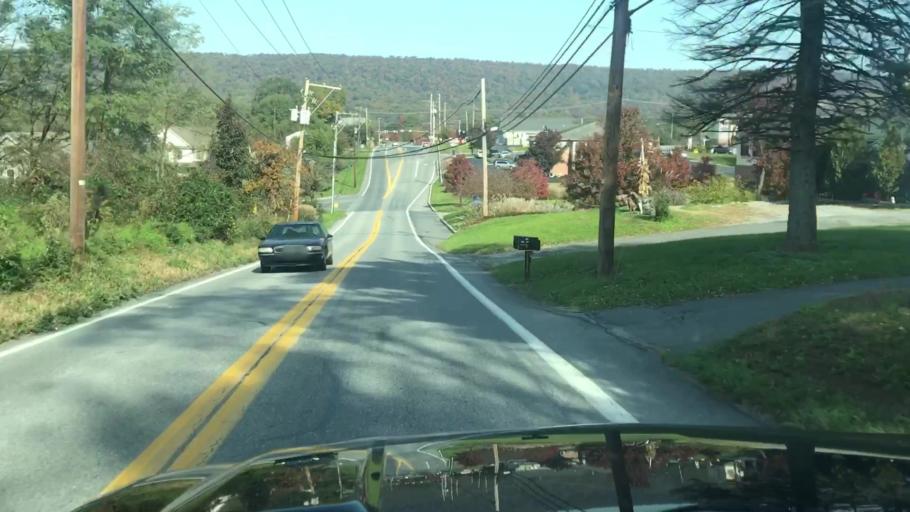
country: US
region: Pennsylvania
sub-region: Cumberland County
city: Enola
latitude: 40.2862
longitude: -76.9865
